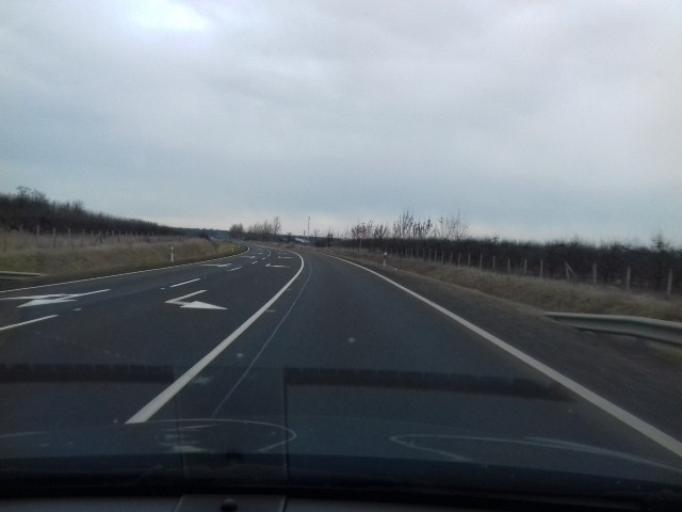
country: HU
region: Szabolcs-Szatmar-Bereg
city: Nyirbogdany
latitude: 48.0198
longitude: 21.8429
